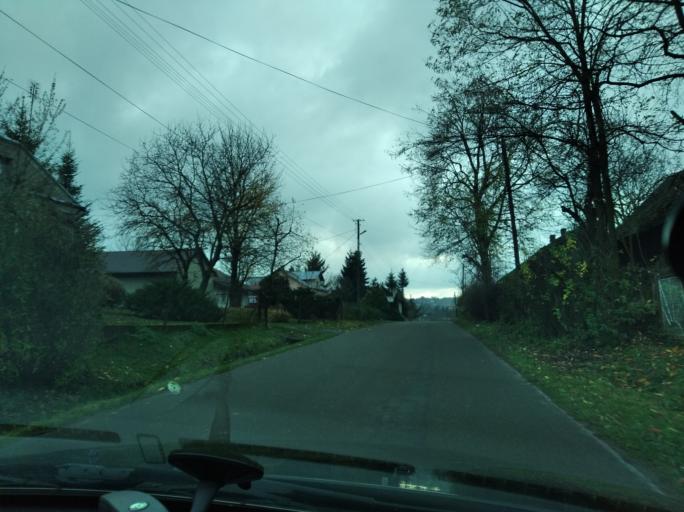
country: PL
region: Subcarpathian Voivodeship
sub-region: Powiat przeworski
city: Sietesz
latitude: 49.9870
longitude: 22.3475
